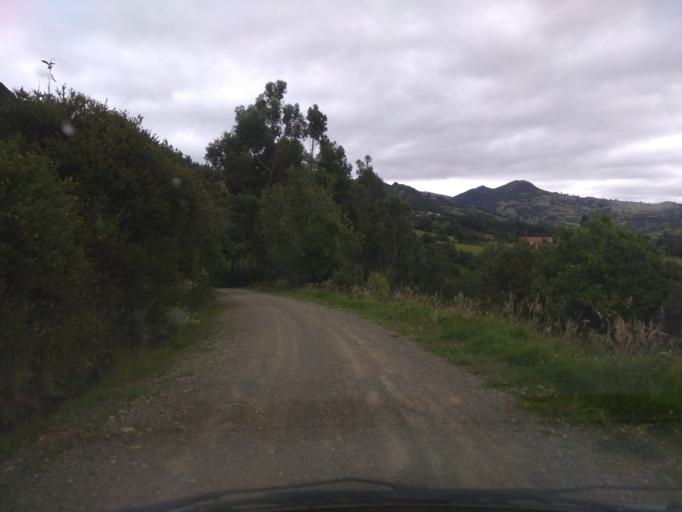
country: CO
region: Boyaca
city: Mongui
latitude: 5.7286
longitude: -72.8387
